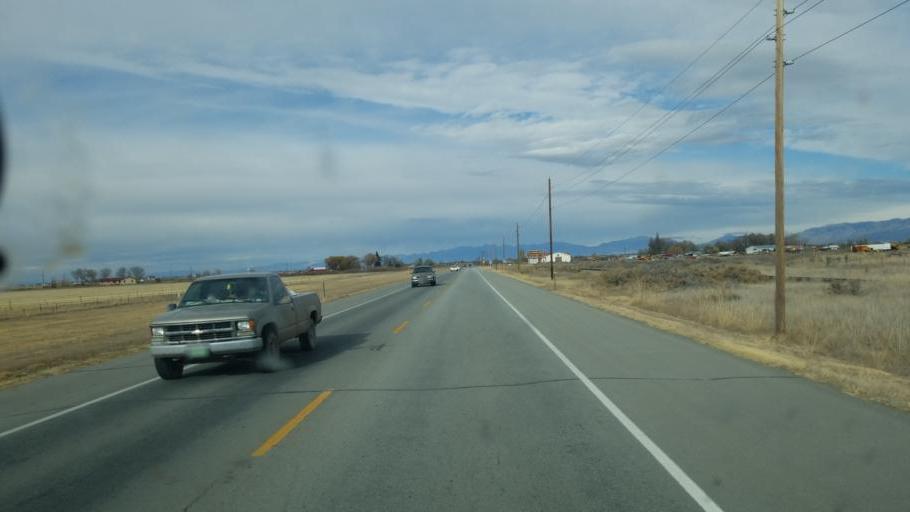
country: US
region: Colorado
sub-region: Alamosa County
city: Alamosa
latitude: 37.4108
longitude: -105.9009
